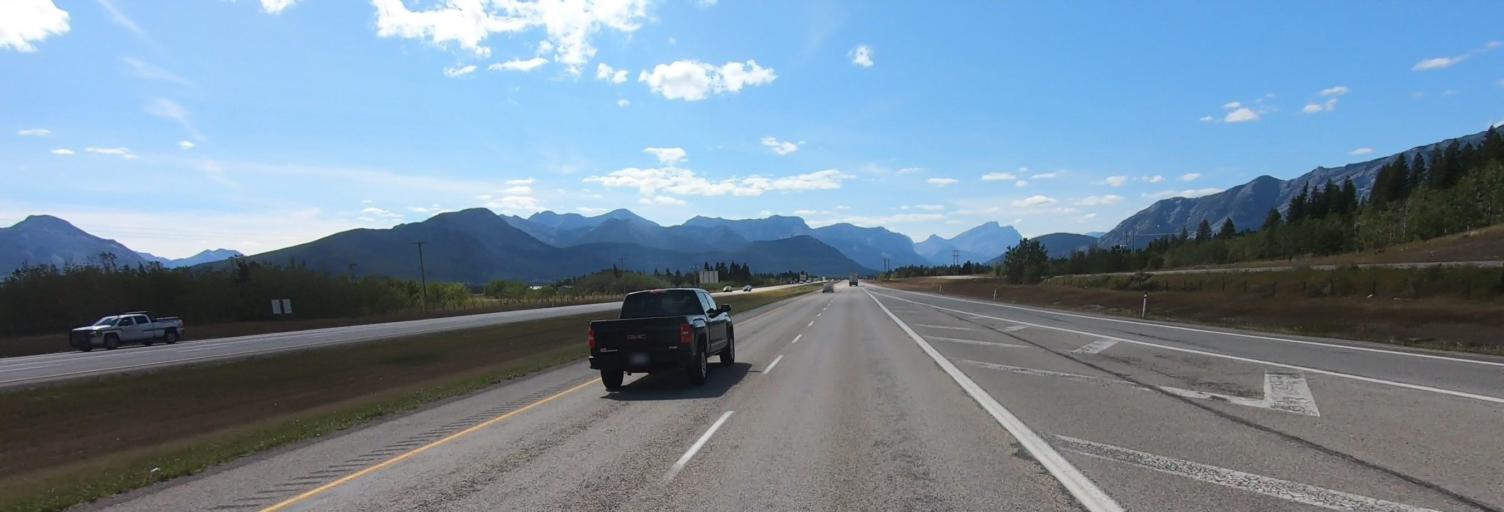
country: CA
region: Alberta
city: Canmore
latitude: 51.1022
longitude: -115.0255
